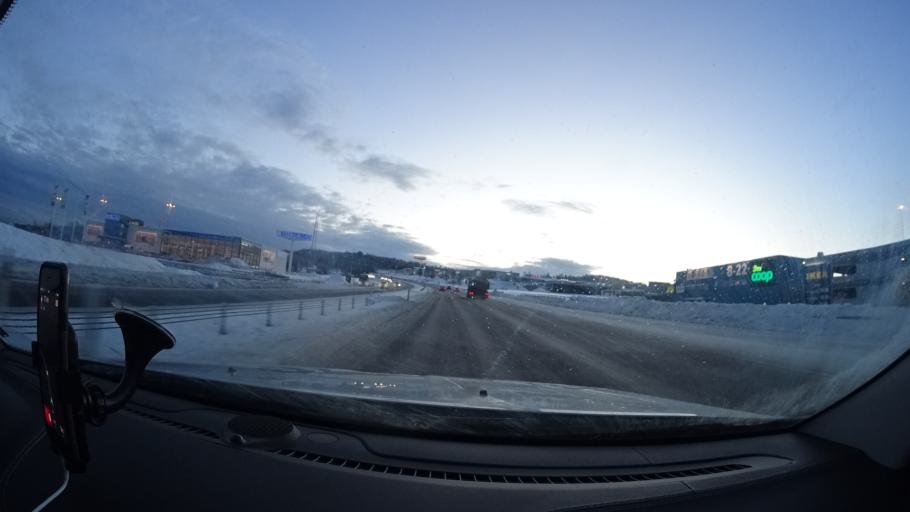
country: SE
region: Vaesternorrland
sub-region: Sundsvalls Kommun
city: Sundsbruk
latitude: 62.4447
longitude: 17.3382
